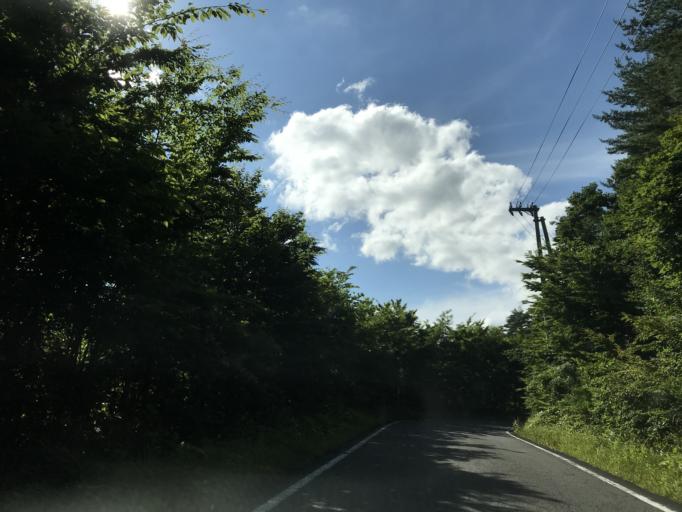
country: JP
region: Iwate
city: Ichinoseki
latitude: 38.9001
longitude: 140.8801
